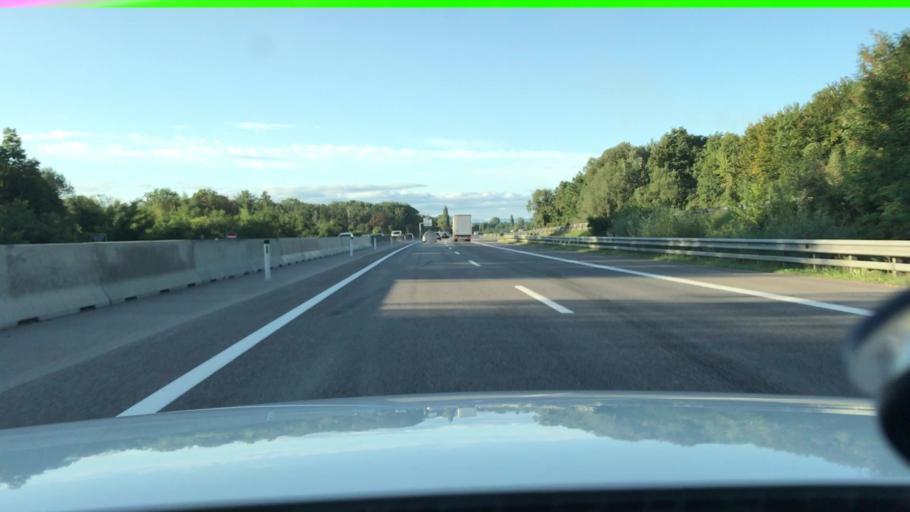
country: AT
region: Lower Austria
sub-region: Politischer Bezirk Sankt Polten
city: Herzogenburg
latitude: 48.2627
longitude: 15.6978
